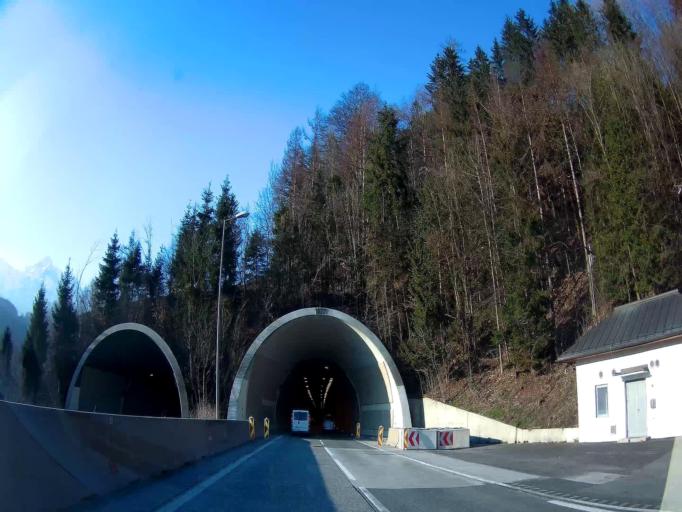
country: AT
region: Salzburg
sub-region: Politischer Bezirk Sankt Johann im Pongau
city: Werfen
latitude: 47.4723
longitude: 13.1982
